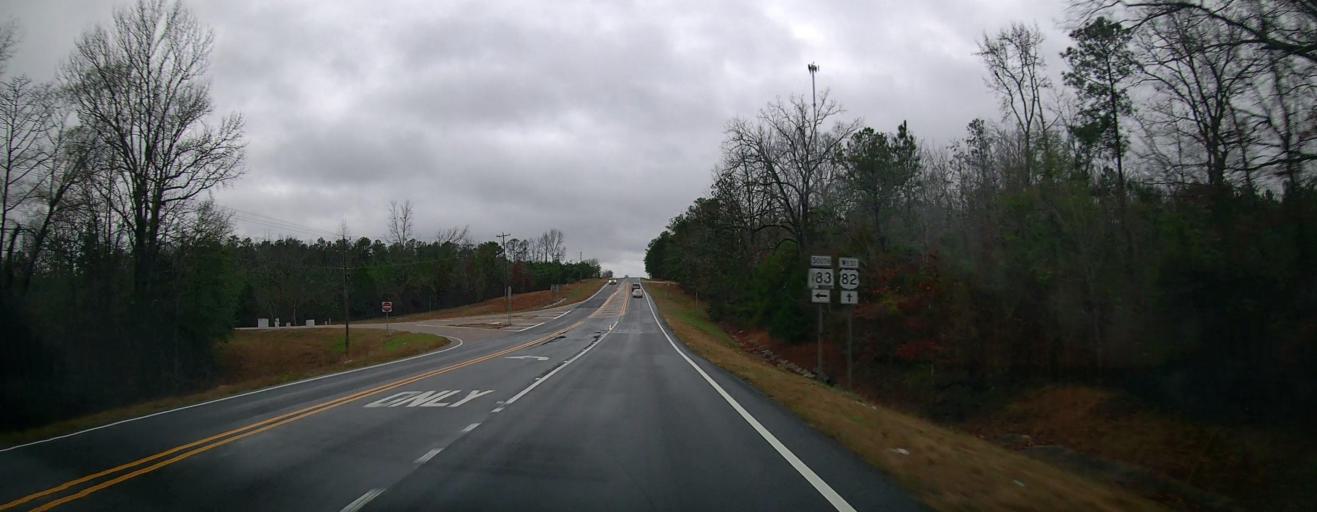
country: US
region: Alabama
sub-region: Bibb County
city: Centreville
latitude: 32.8132
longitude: -86.9316
